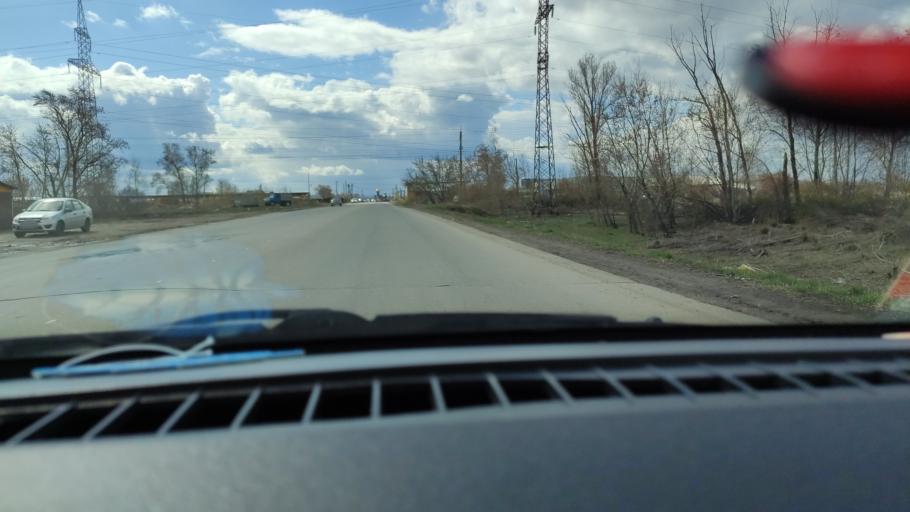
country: RU
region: Samara
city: Tol'yatti
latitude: 53.5790
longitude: 49.4029
